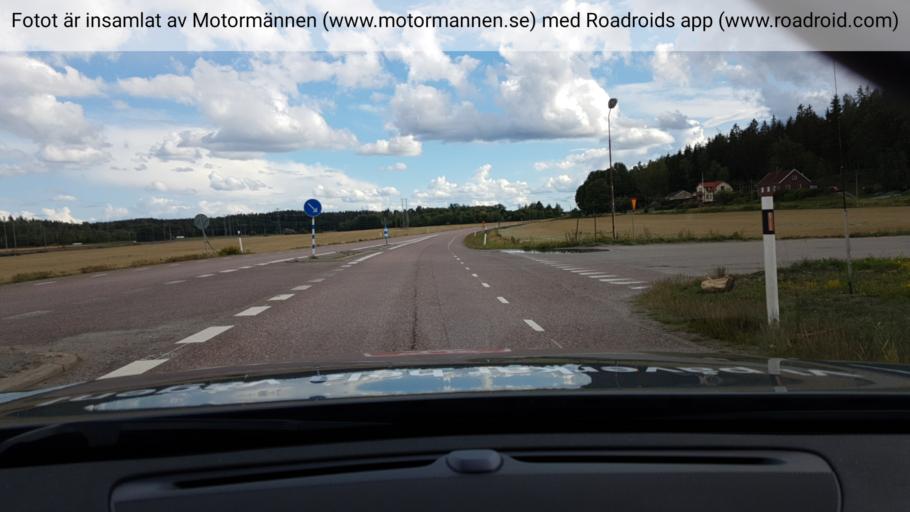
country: SE
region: Soedermanland
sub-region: Strangnas Kommun
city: Strangnas
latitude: 59.3329
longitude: 17.0665
